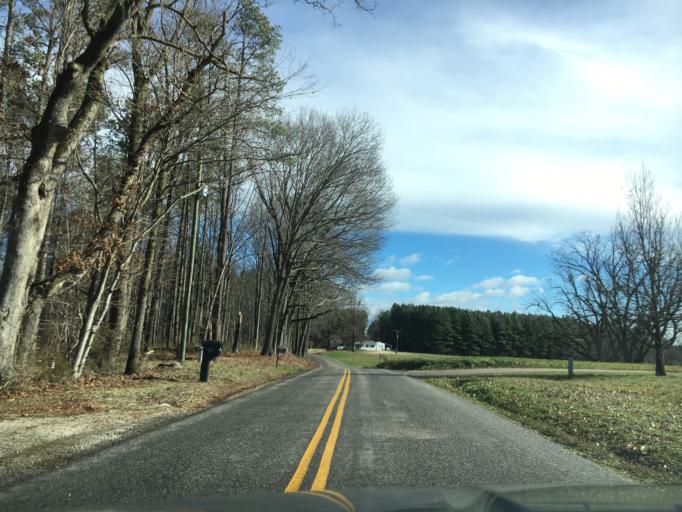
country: US
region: Virginia
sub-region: Amelia County
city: Amelia Court House
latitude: 37.4445
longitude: -78.0080
